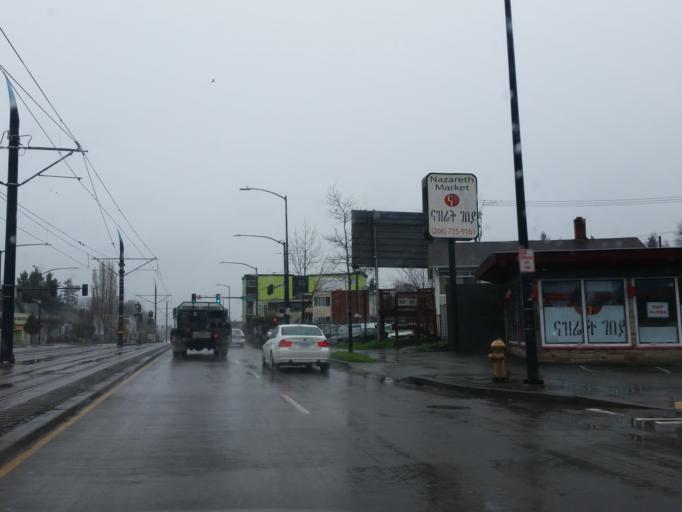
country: US
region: Washington
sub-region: King County
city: Riverton
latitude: 47.5526
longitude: -122.2886
